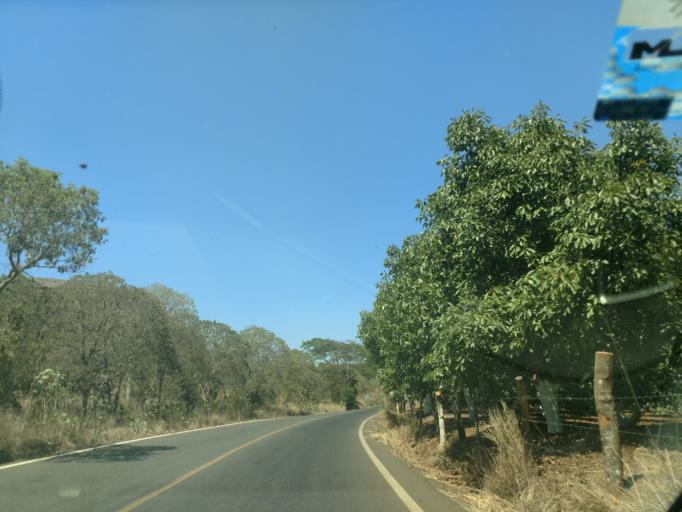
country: MX
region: Nayarit
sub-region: Tepic
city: La Corregidora
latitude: 21.4993
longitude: -104.7765
